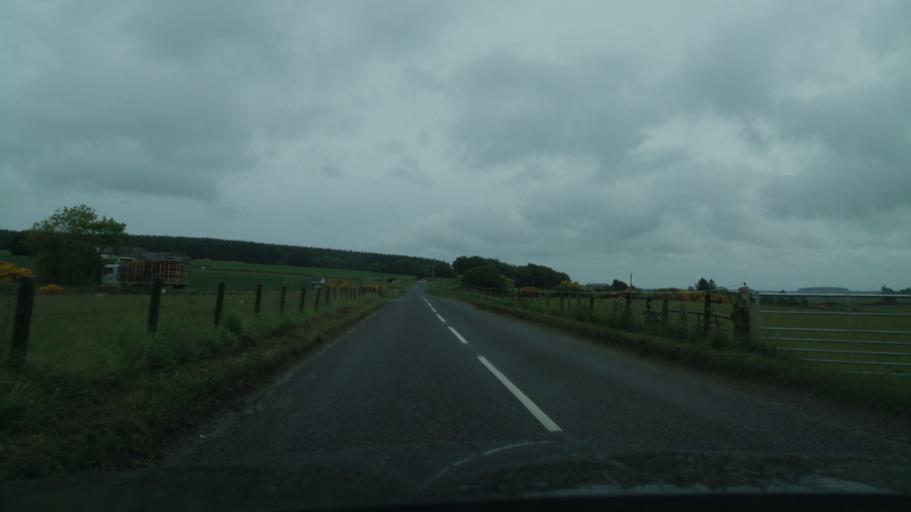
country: GB
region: Scotland
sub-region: Aberdeenshire
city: Portsoy
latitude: 57.5977
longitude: -2.7310
